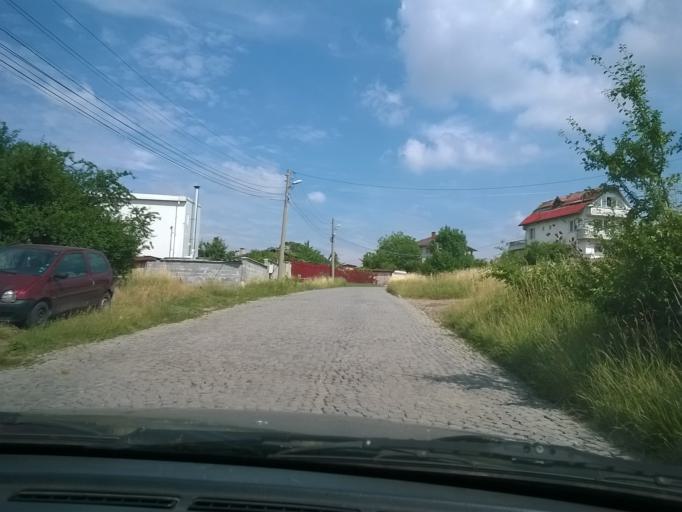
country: BG
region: Sofiya
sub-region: Obshtina Bozhurishte
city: Bozhurishte
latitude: 42.6824
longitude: 23.2384
